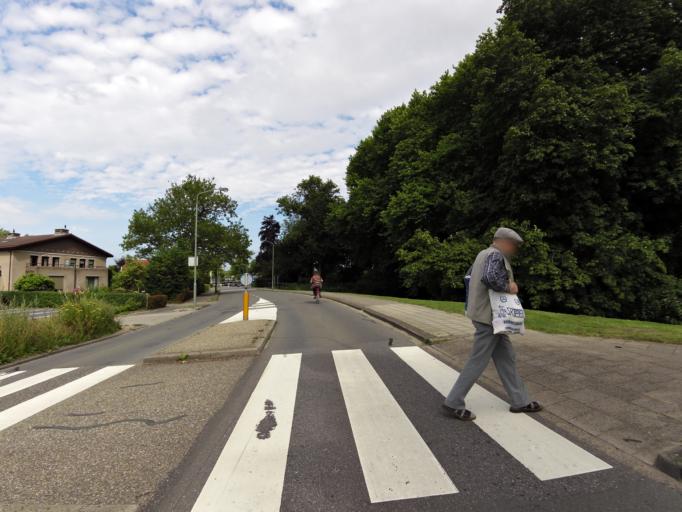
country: NL
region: South Holland
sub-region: Gemeente Dordrecht
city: Dordrecht
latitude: 51.7936
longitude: 4.7012
